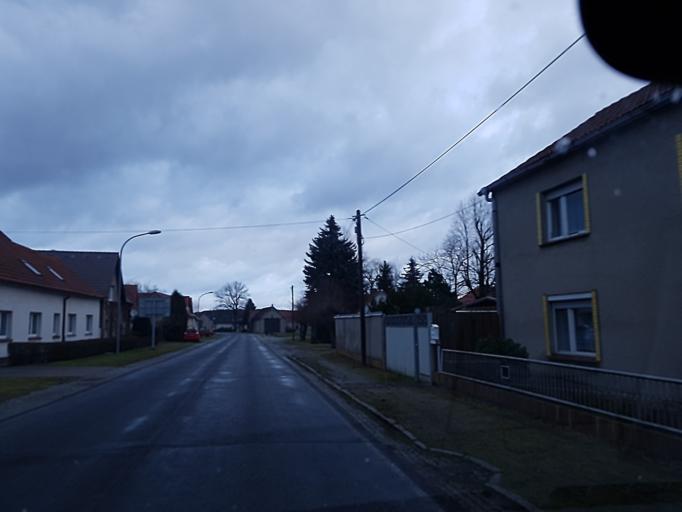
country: DE
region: Brandenburg
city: Plessa
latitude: 51.5351
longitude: 13.6652
